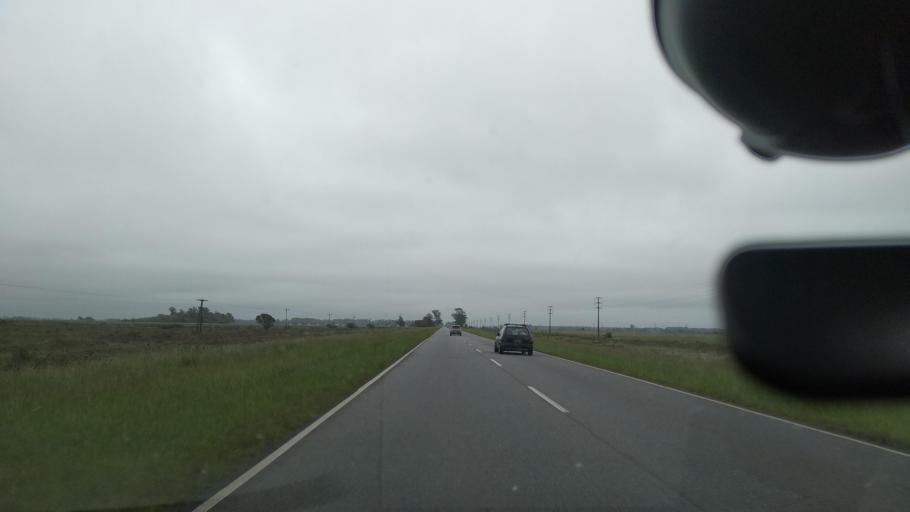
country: AR
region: Buenos Aires
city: Veronica
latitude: -35.3423
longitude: -57.4482
